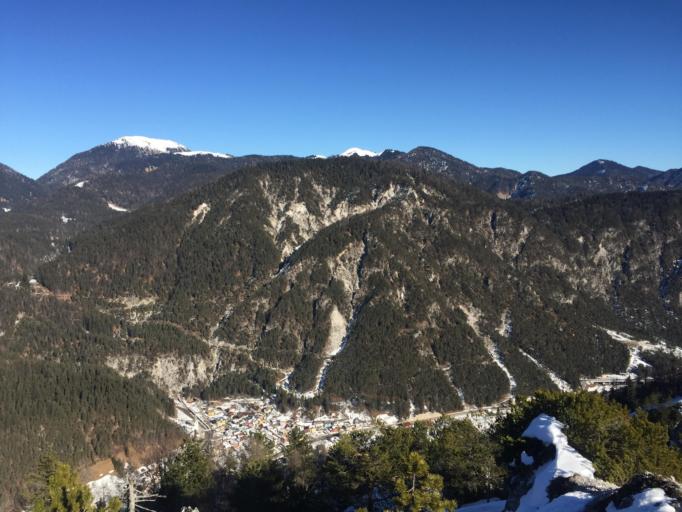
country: IT
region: Friuli Venezia Giulia
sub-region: Provincia di Udine
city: Malborghetto
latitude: 46.5032
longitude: 13.4666
